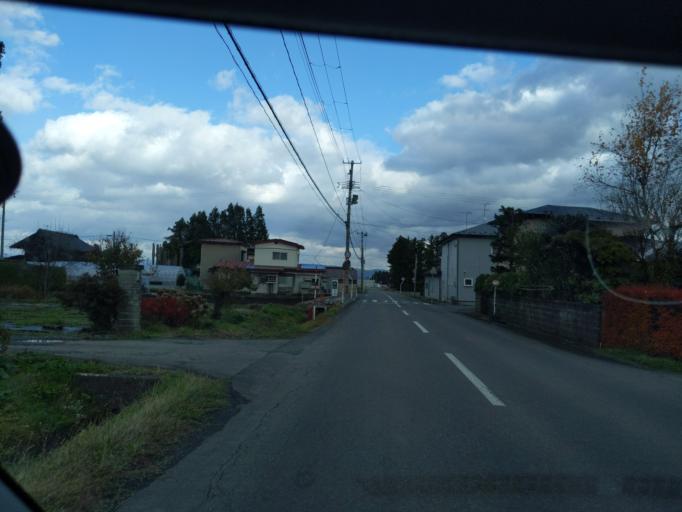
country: JP
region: Iwate
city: Mizusawa
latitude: 39.1267
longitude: 141.0871
